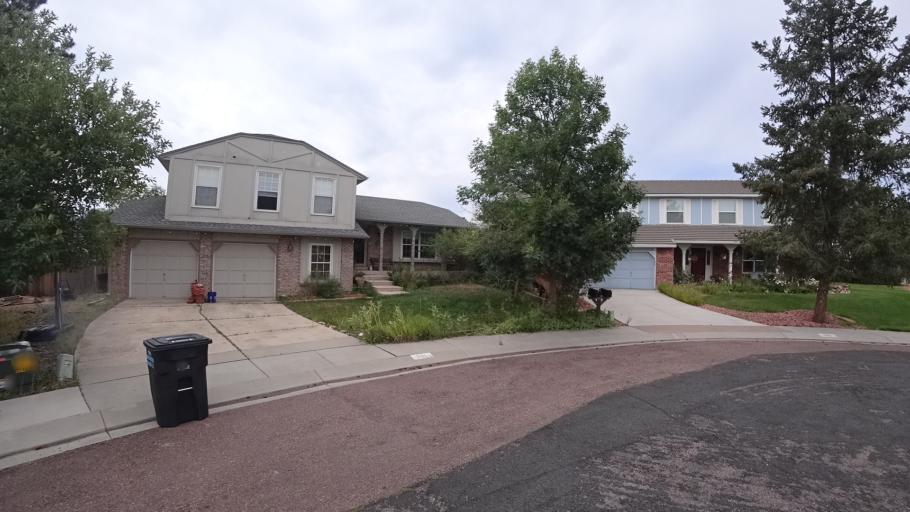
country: US
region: Colorado
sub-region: El Paso County
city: Air Force Academy
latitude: 38.9223
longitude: -104.8374
